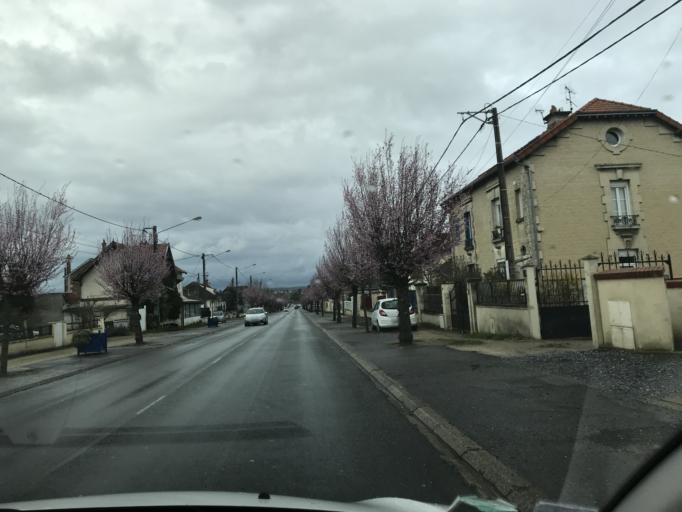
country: FR
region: Picardie
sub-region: Departement de l'Aisne
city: Belleu
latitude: 49.3640
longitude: 3.3377
